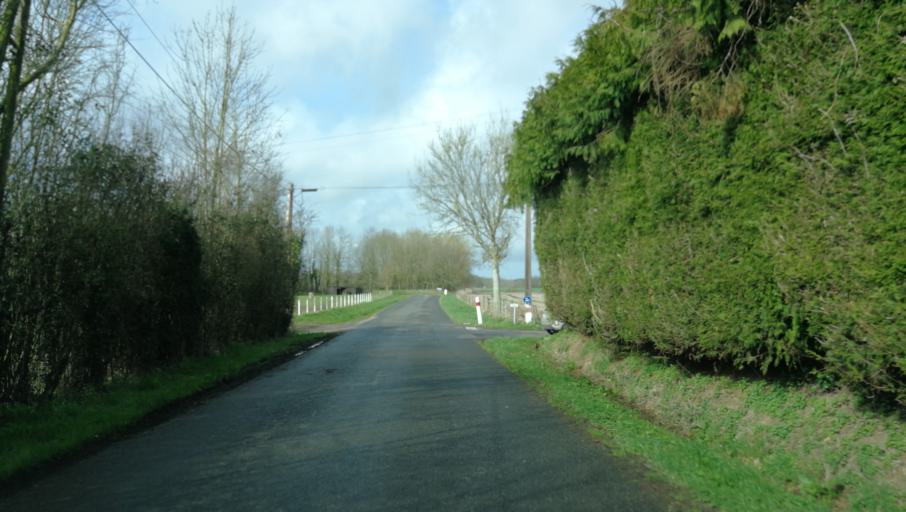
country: FR
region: Haute-Normandie
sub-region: Departement de l'Eure
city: Lieurey
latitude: 49.2459
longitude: 0.4710
